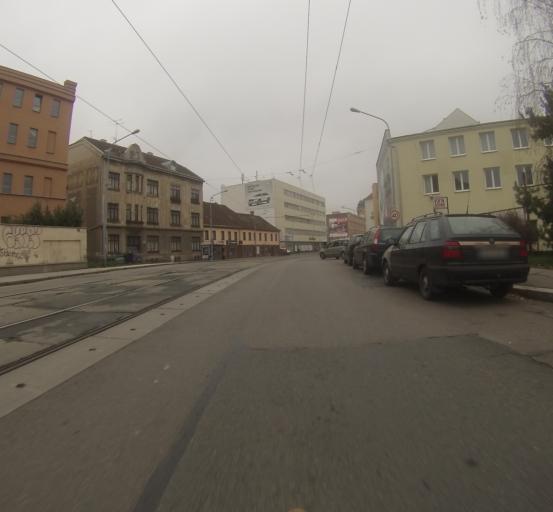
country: CZ
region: South Moravian
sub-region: Mesto Brno
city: Brno
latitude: 49.2016
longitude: 16.6317
